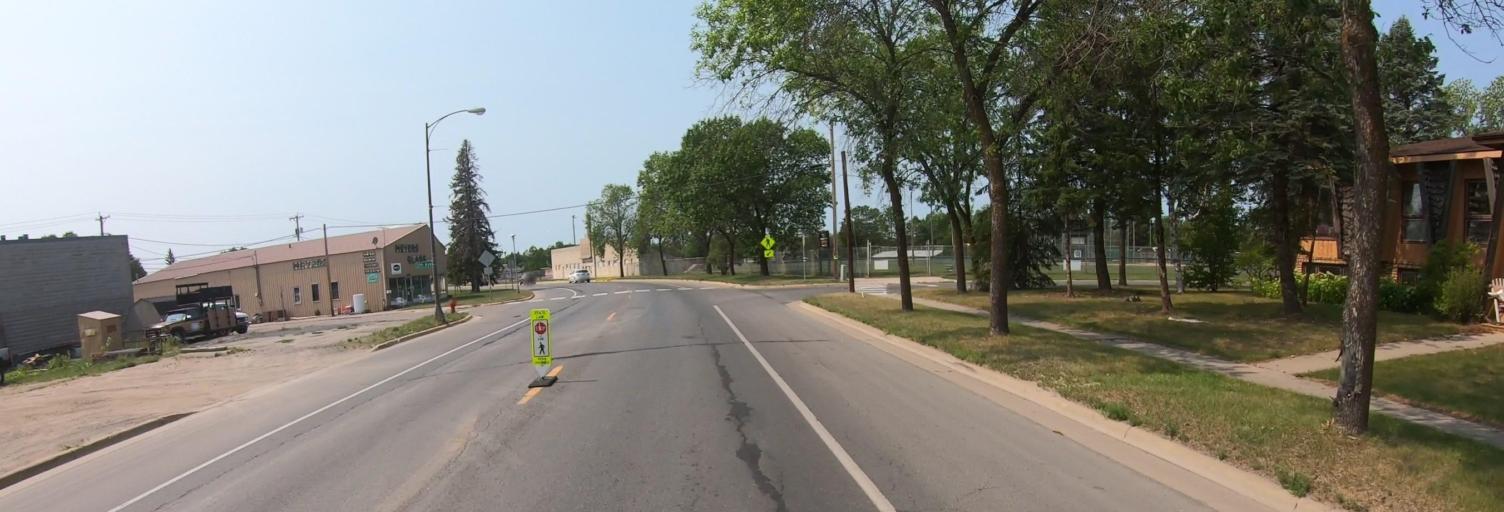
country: US
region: Minnesota
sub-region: Koochiching County
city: International Falls
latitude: 48.6008
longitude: -93.4168
